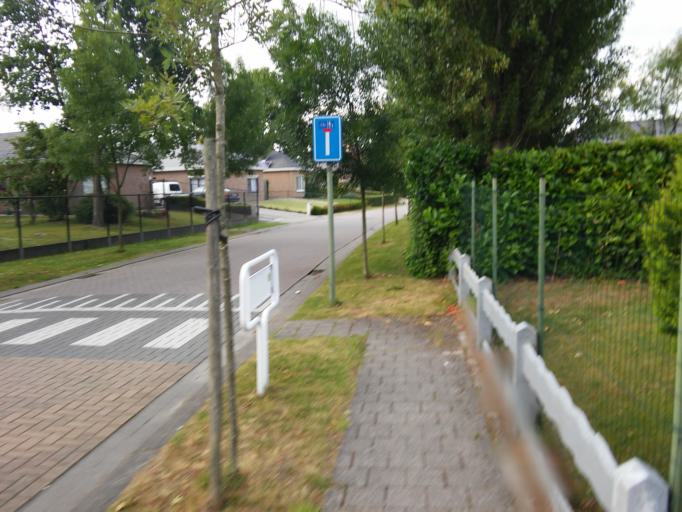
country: BE
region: Flanders
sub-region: Provincie Antwerpen
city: Rumst
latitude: 51.0862
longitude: 4.4358
